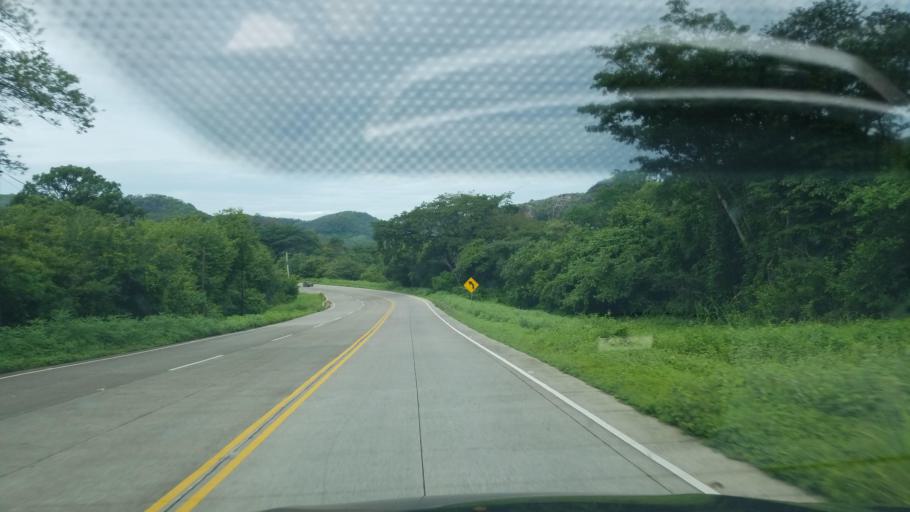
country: HN
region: Francisco Morazan
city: El Porvenir
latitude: 13.6952
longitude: -87.3273
